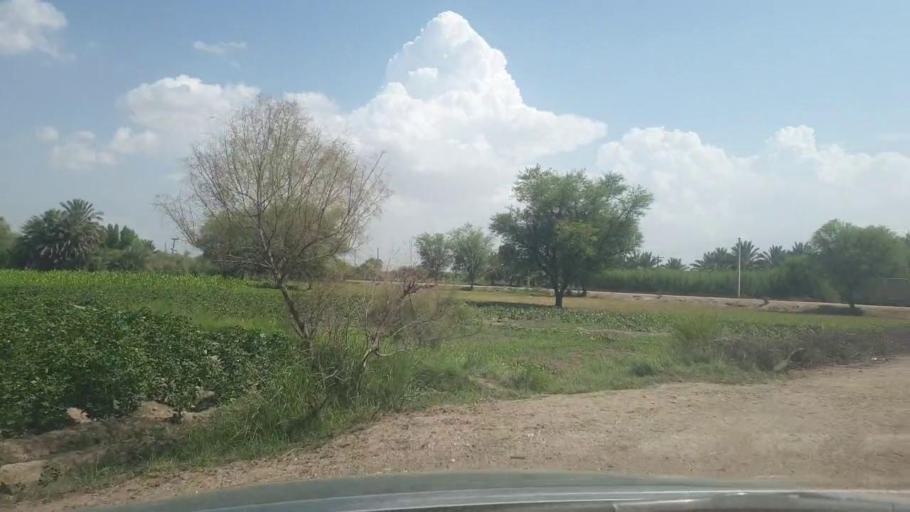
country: PK
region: Sindh
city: Khairpur
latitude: 27.5477
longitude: 68.8026
